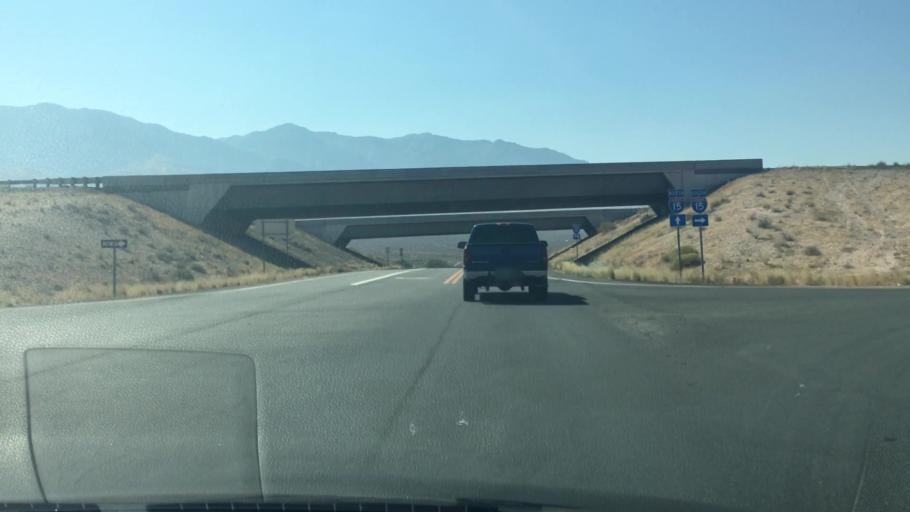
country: US
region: Arizona
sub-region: Mohave County
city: Beaver Dam
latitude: 36.8926
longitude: -113.9300
